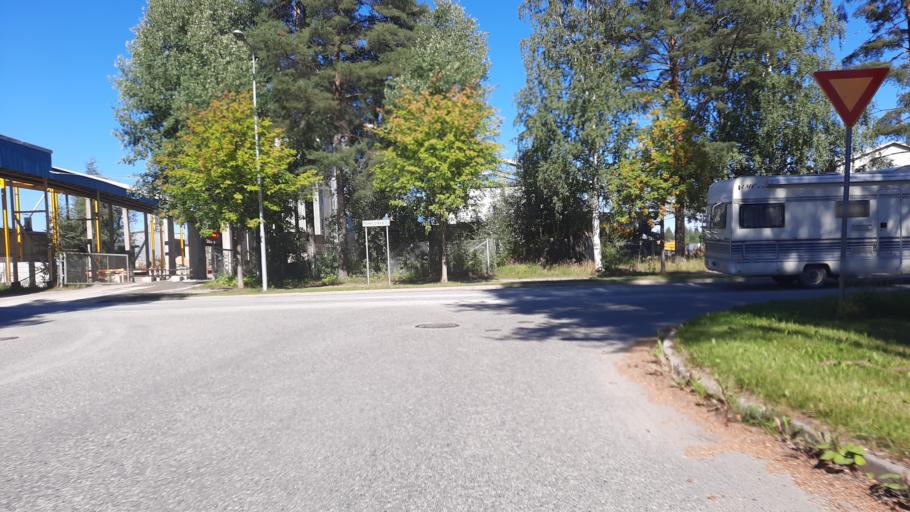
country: FI
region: North Karelia
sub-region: Joensuu
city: Joensuu
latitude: 62.6211
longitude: 29.7562
